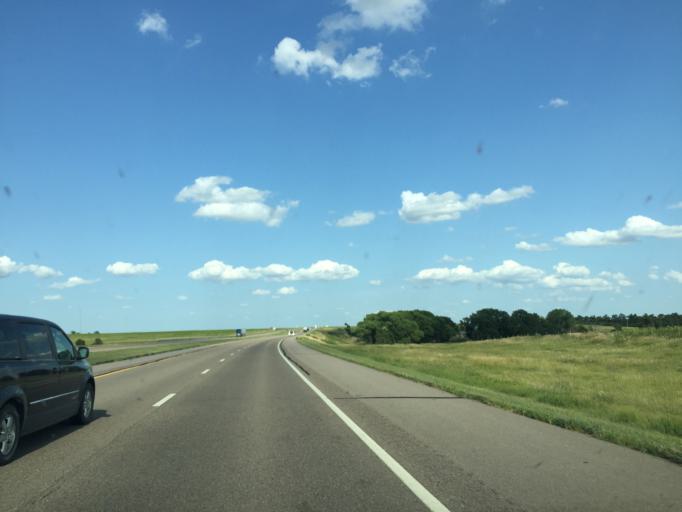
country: US
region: Kansas
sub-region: Trego County
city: WaKeeney
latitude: 39.0233
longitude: -100.0075
